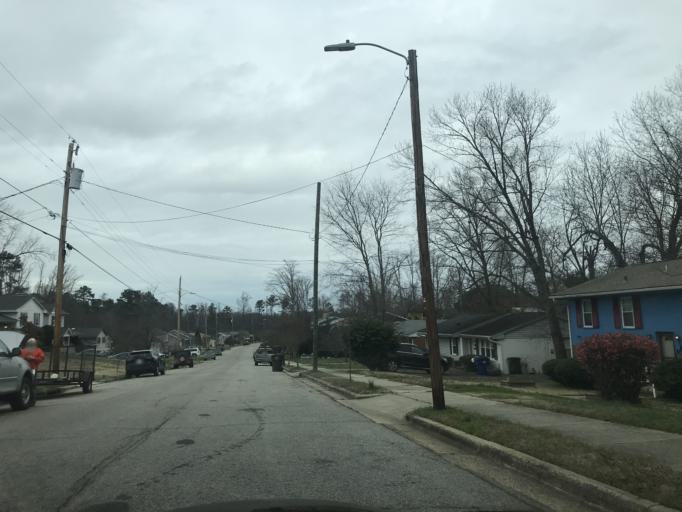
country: US
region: North Carolina
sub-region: Wake County
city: Raleigh
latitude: 35.7981
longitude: -78.6033
